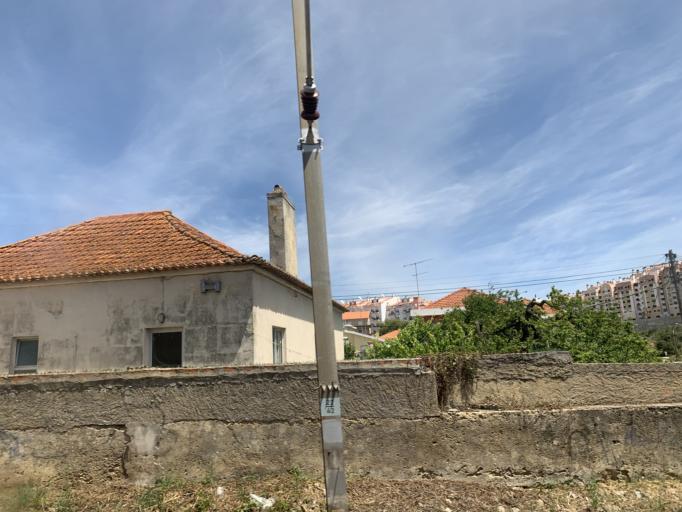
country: PT
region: Lisbon
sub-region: Sintra
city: Rio de Mouro
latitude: 38.7979
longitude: -9.3376
